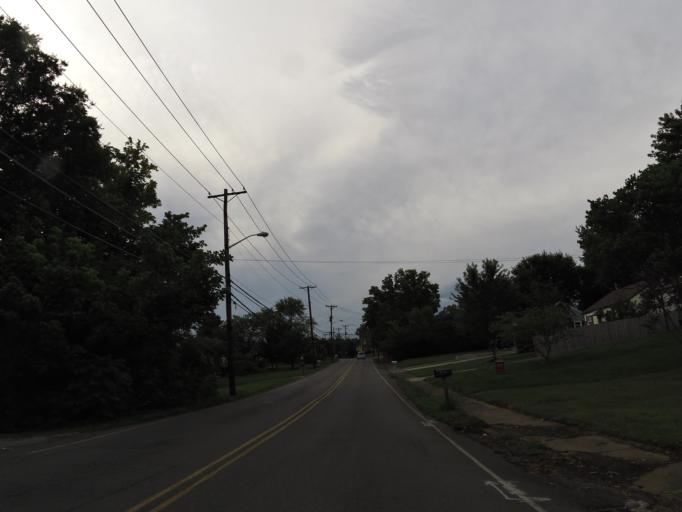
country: US
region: Tennessee
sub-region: Knox County
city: Knoxville
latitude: 36.0082
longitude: -83.9131
